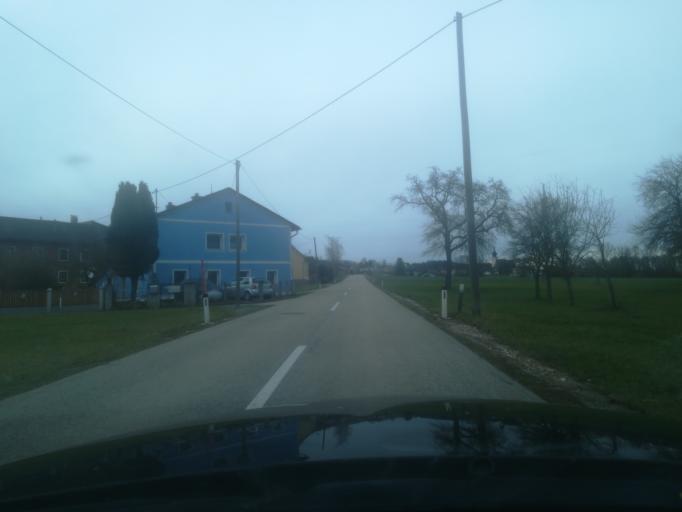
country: AT
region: Upper Austria
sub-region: Wels-Land
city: Neukirchen bei Lambach
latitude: 48.0963
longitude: 13.8217
